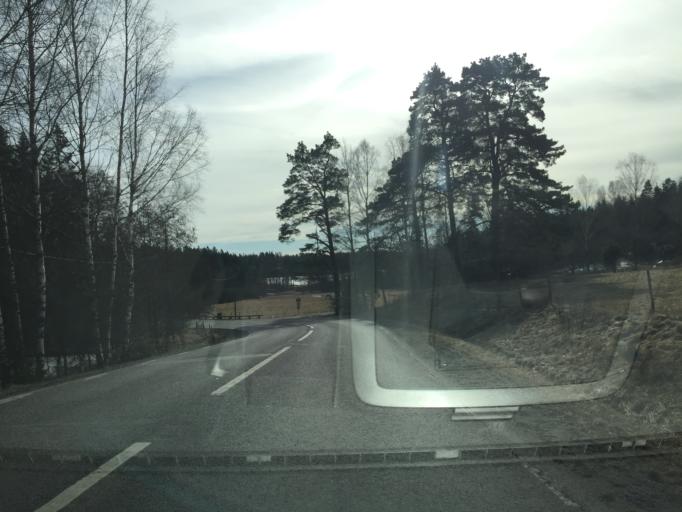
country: SE
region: Stockholm
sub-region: Huddinge Kommun
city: Huddinge
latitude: 59.1308
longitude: 17.9893
